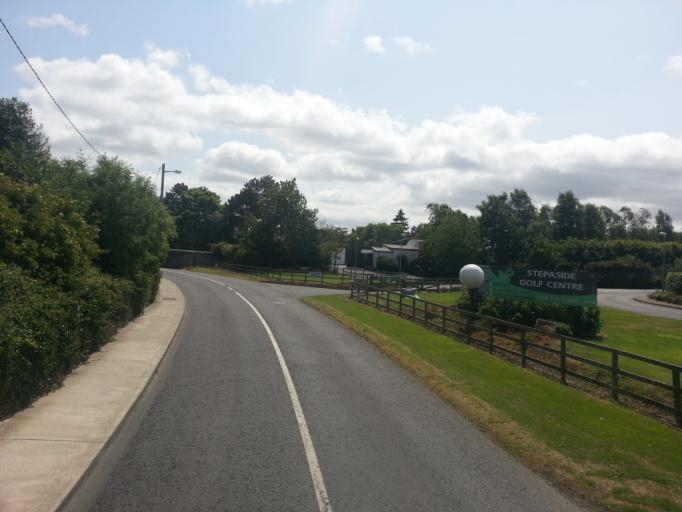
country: IE
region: Leinster
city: Sandyford
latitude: 53.2474
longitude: -6.2035
